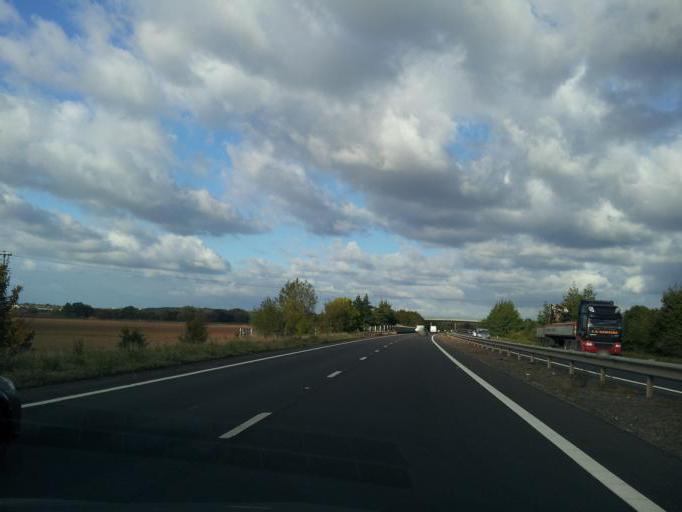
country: GB
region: England
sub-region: Bedford
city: Cardington
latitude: 52.1359
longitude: -0.4108
